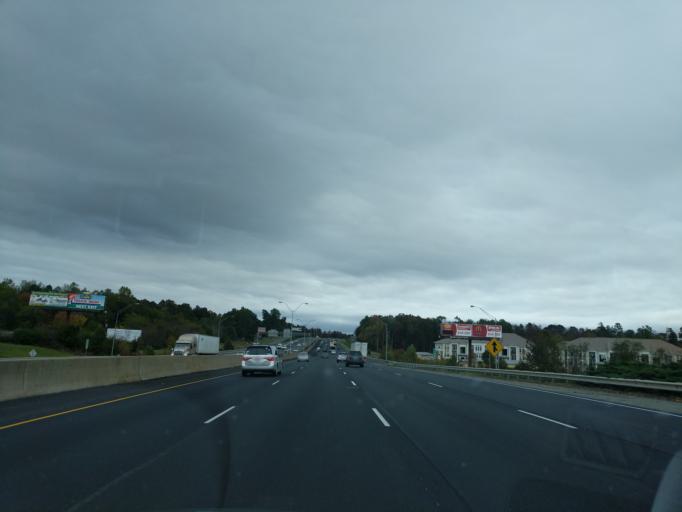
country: US
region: North Carolina
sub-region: Alamance County
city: Graham
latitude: 36.0631
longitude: -79.3841
